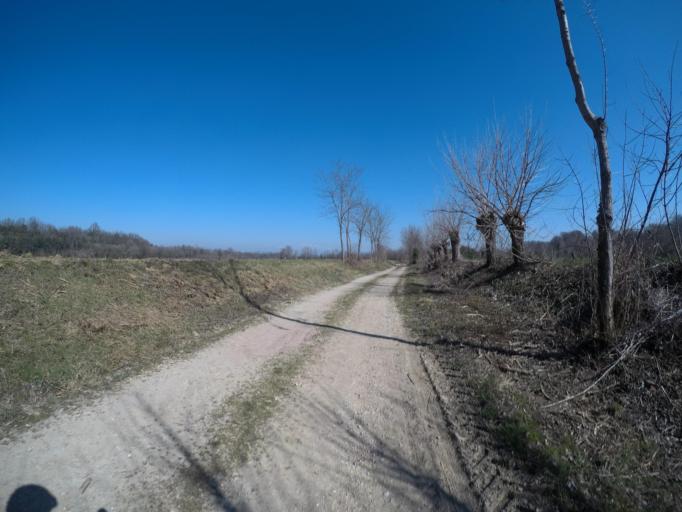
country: IT
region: Friuli Venezia Giulia
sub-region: Provincia di Udine
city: Pozzuolo del Friuli
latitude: 45.9903
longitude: 13.1888
